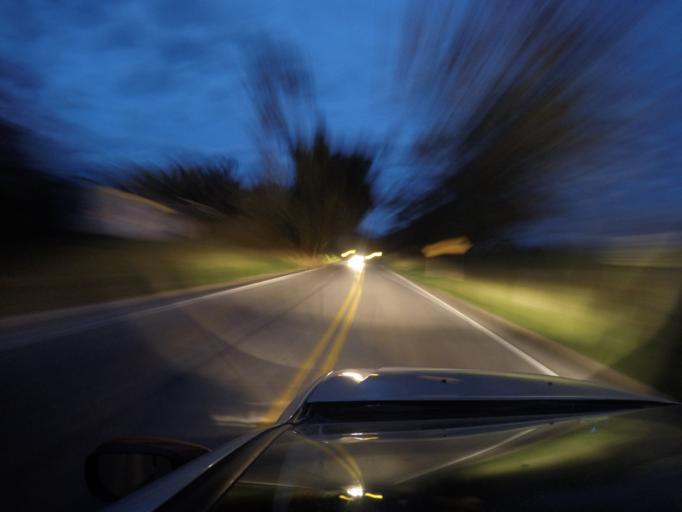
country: CO
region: Tolima
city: Fresno
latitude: 5.1580
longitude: -75.0795
